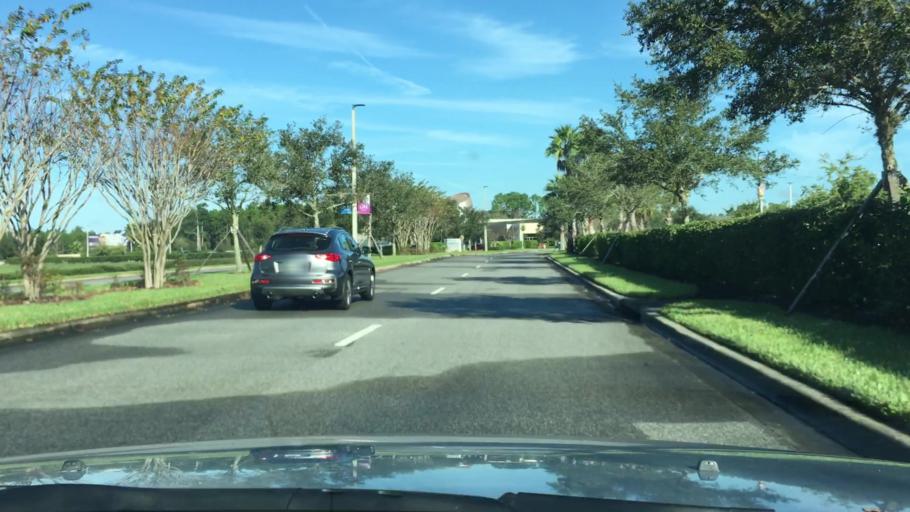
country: US
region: Florida
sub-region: Volusia County
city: Ormond Beach
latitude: 29.2434
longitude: -81.1095
